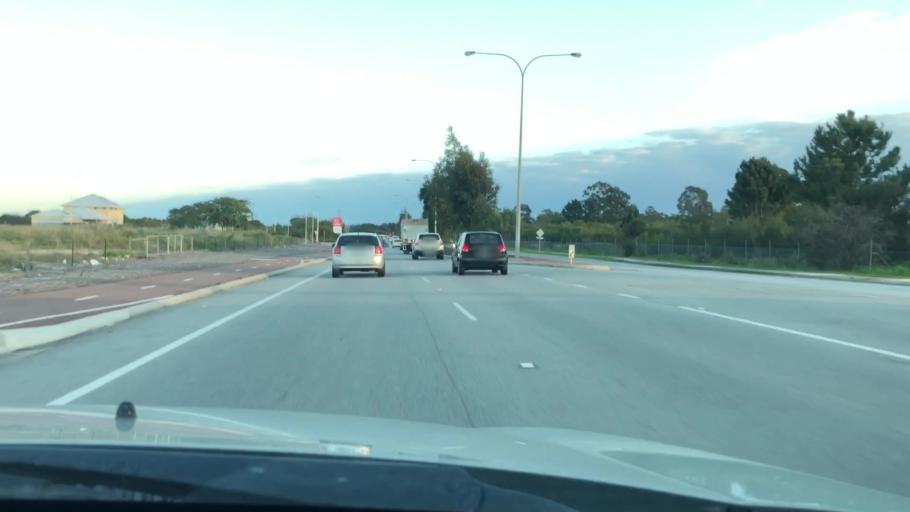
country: AU
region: Western Australia
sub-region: Armadale
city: Harrisdale
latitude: -32.1042
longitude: 115.9350
